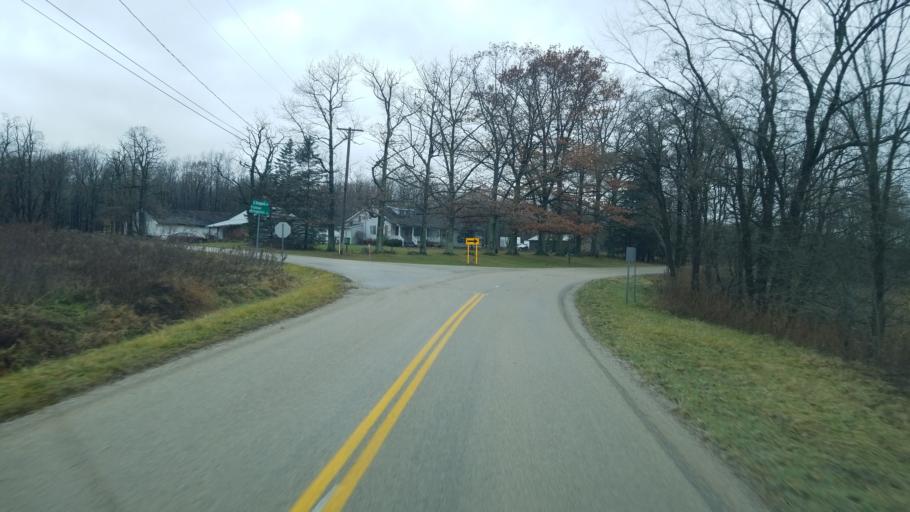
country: US
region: Ohio
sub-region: Ashtabula County
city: Andover
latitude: 41.7239
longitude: -80.6270
